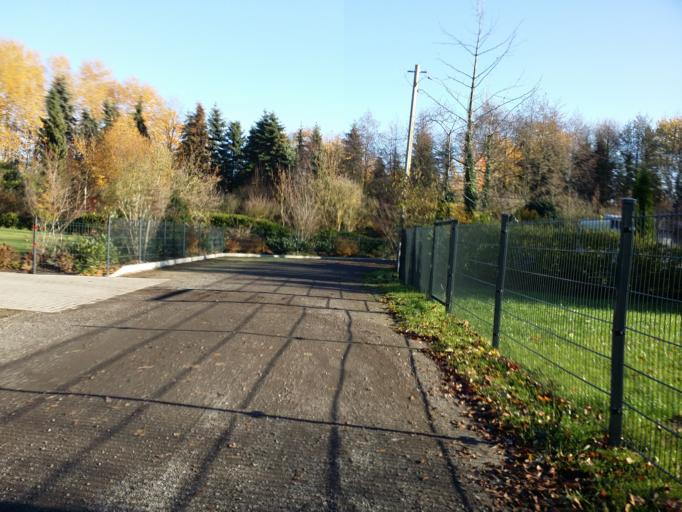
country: DE
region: Lower Saxony
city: Oyten
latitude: 53.0747
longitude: 8.9699
